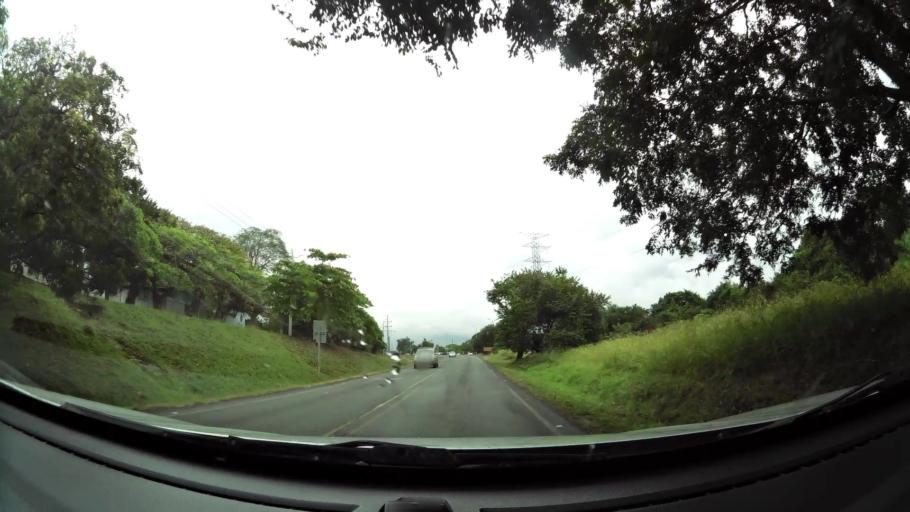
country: CR
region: Puntarenas
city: Esparza
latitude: 9.9935
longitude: -84.7082
